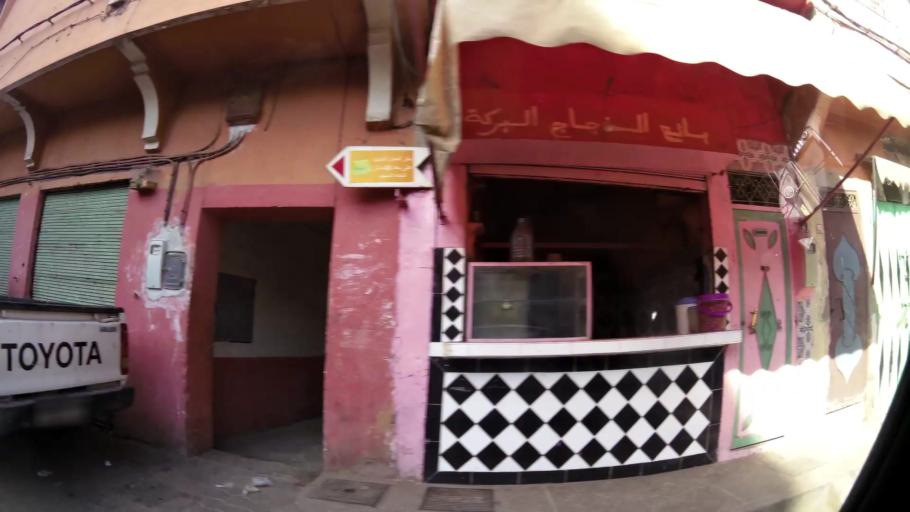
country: MA
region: Marrakech-Tensift-Al Haouz
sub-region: Marrakech
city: Marrakesh
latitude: 31.6143
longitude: -7.9629
